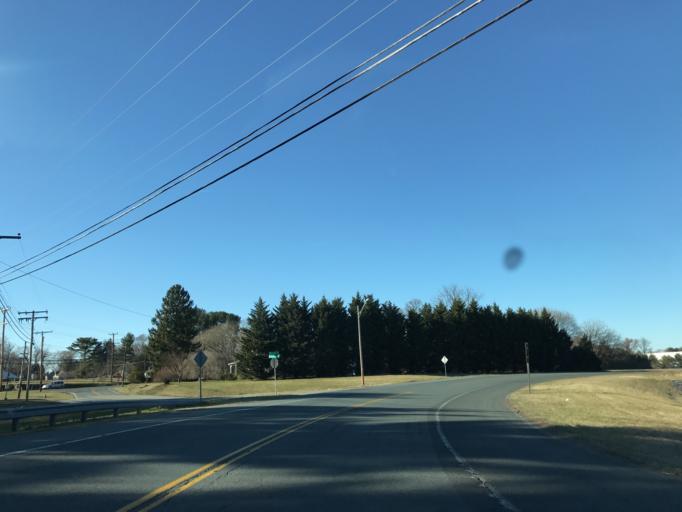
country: US
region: Maryland
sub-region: Harford County
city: Perryman
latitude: 39.4671
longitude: -76.2029
